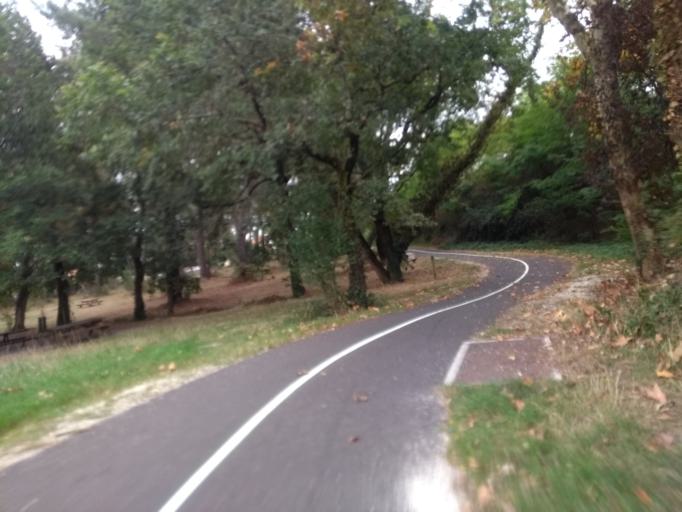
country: FR
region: Aquitaine
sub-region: Departement de la Gironde
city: Pessac
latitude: 44.7885
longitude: -0.6408
